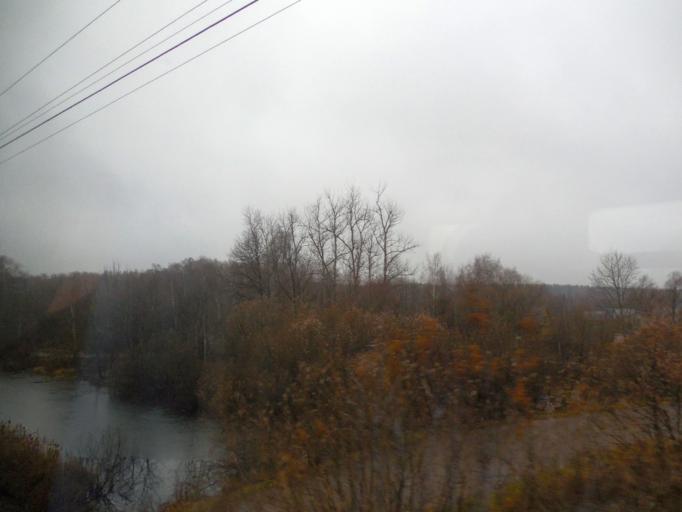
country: RU
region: Moskovskaya
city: Vostryakovo
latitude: 55.3729
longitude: 37.8220
